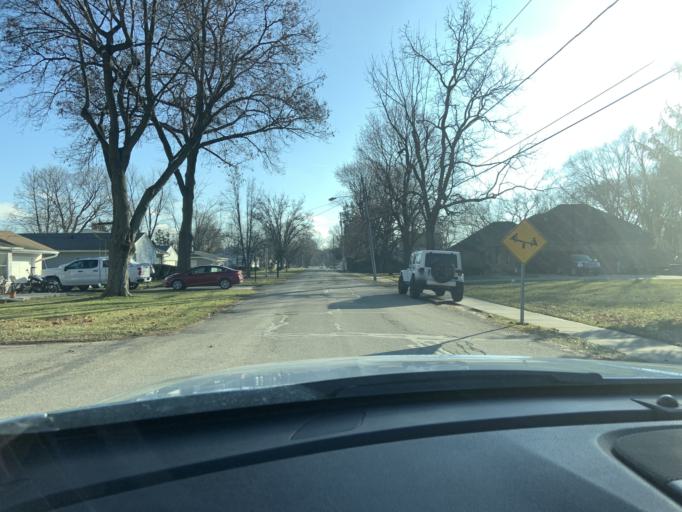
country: US
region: Illinois
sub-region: LaSalle County
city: Seneca
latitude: 41.3109
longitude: -88.6065
